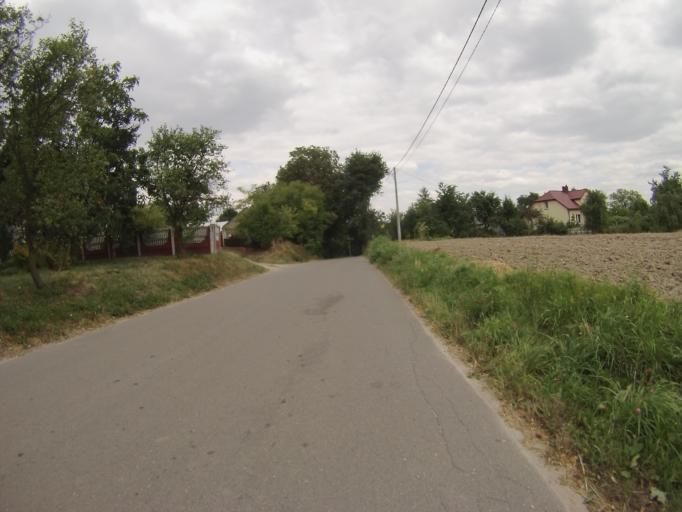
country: PL
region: Swietokrzyskie
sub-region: Powiat staszowski
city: Bogoria
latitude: 50.6831
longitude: 21.2195
